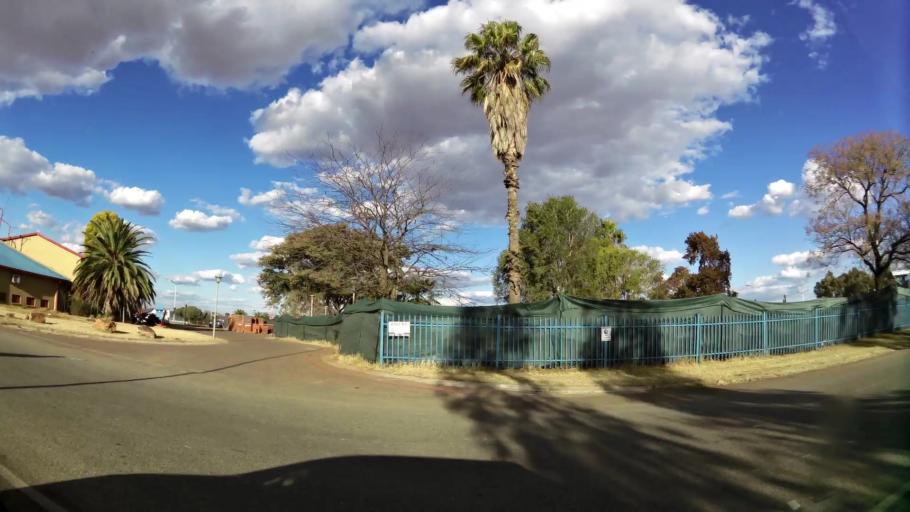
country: ZA
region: North-West
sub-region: Dr Kenneth Kaunda District Municipality
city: Potchefstroom
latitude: -26.7181
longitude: 27.0826
